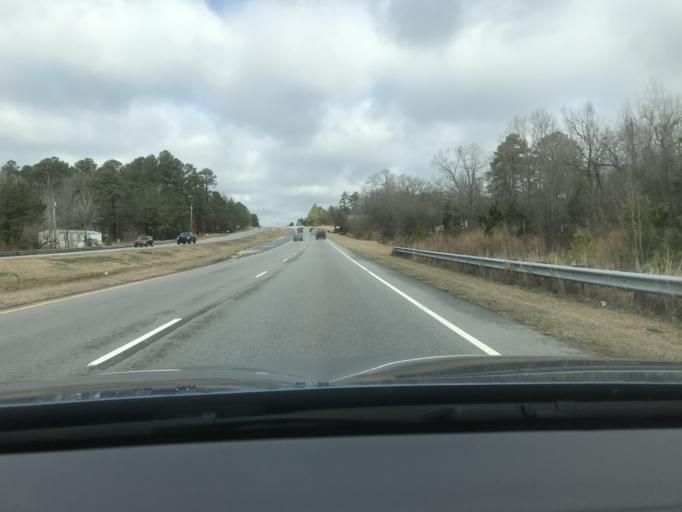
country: US
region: North Carolina
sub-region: Cumberland County
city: Spring Lake
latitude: 35.2863
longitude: -79.0755
